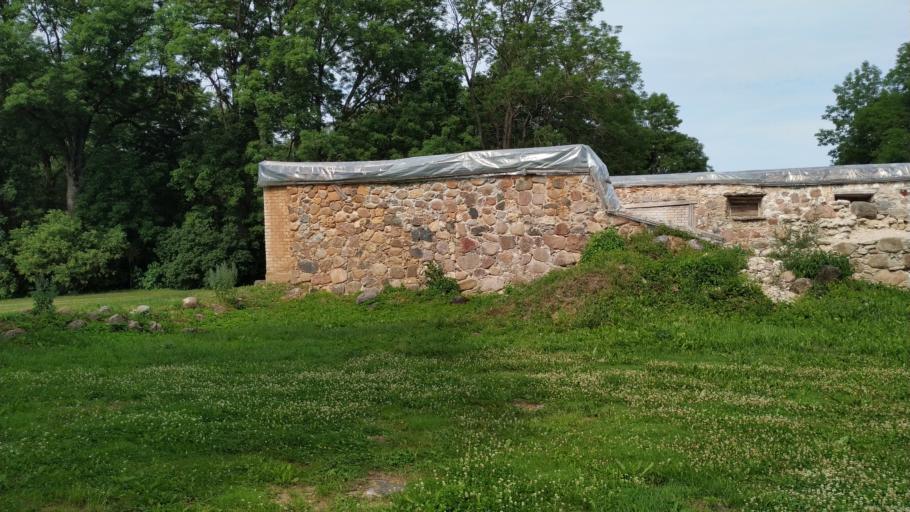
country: LT
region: Panevezys
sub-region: Birzai
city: Birzai
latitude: 56.2149
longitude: 24.6832
